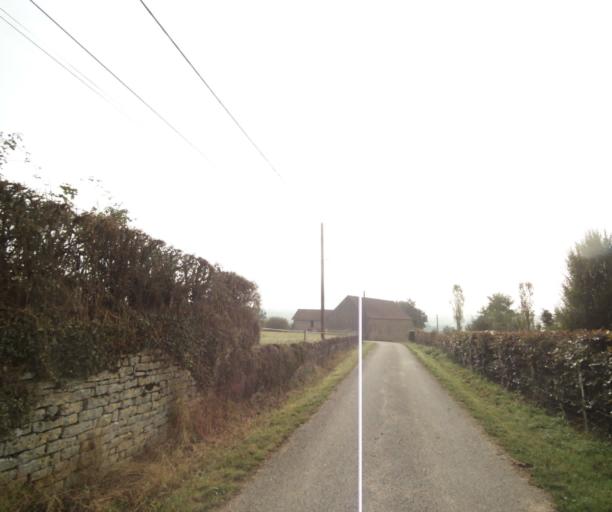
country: FR
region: Bourgogne
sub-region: Departement de Saone-et-Loire
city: Charolles
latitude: 46.4586
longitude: 4.2959
